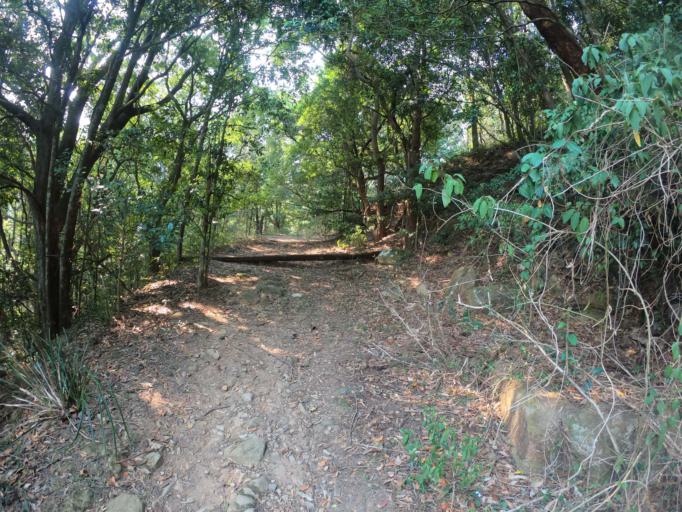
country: AU
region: New South Wales
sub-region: Wollongong
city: Bulli
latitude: -34.3254
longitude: 150.8888
